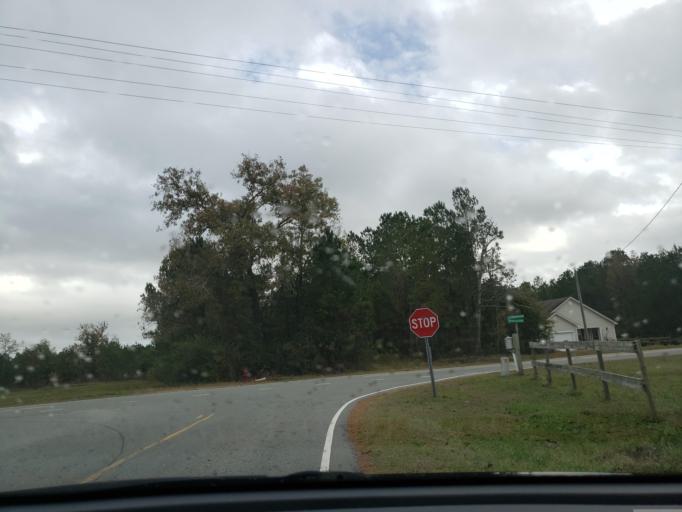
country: US
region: North Carolina
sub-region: Onslow County
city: Richlands
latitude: 34.7355
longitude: -77.6220
